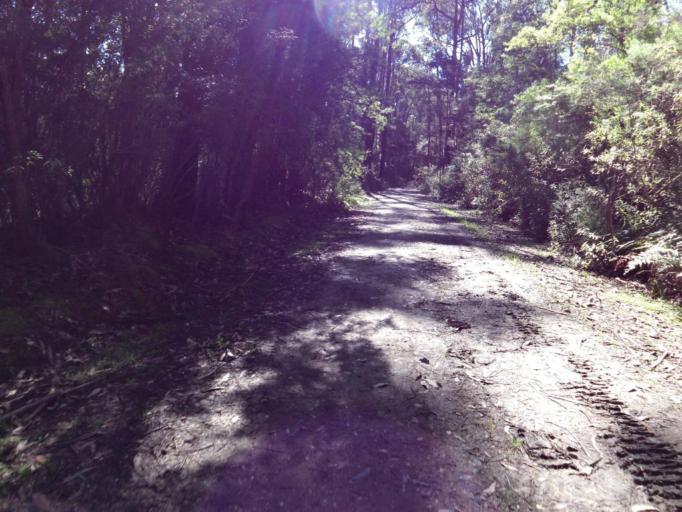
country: AU
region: Victoria
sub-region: Baw Baw
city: Warragul
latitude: -38.0590
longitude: 145.9487
